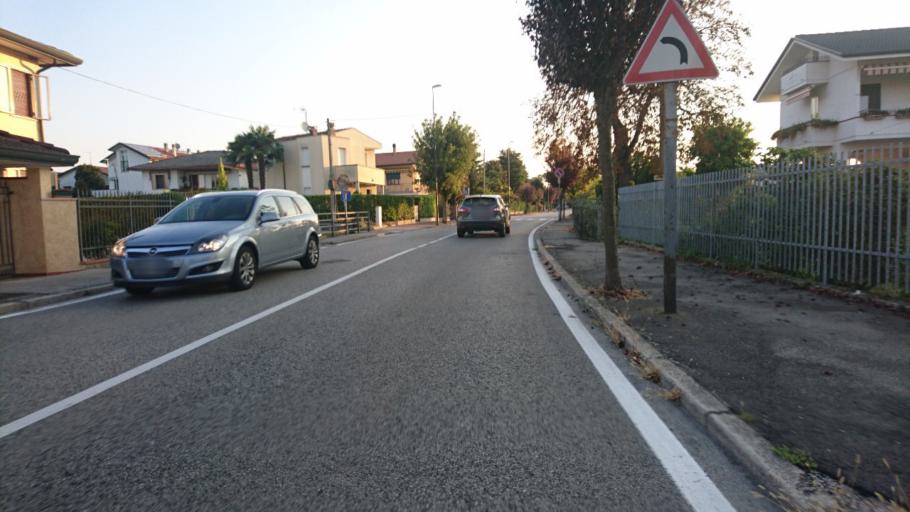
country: IT
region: Veneto
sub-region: Provincia di Padova
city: Ponte San Nicolo
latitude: 45.3681
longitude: 11.9384
